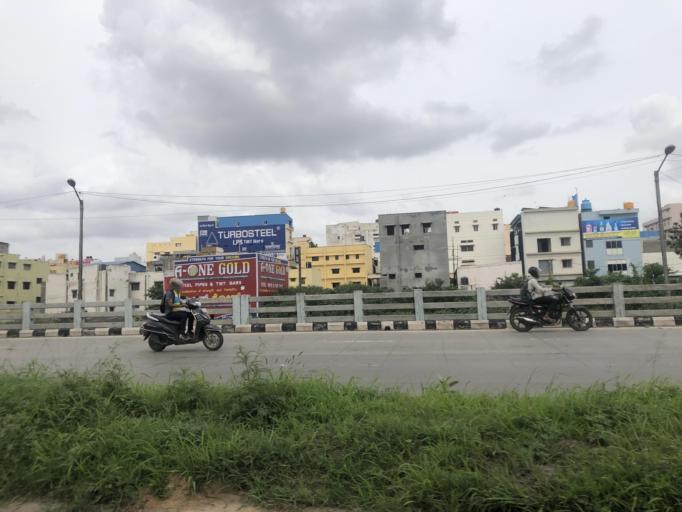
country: IN
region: Karnataka
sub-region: Bangalore Urban
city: Bangalore
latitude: 12.9844
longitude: 77.5188
